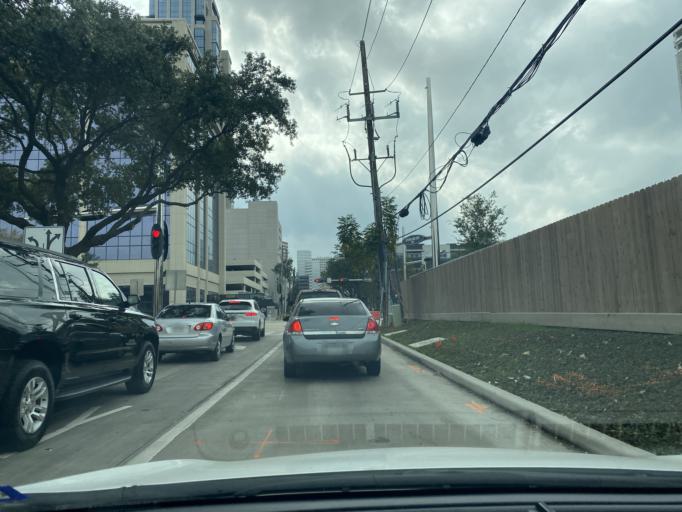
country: US
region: Texas
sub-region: Harris County
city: Hunters Creek Village
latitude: 29.7542
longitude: -95.4578
